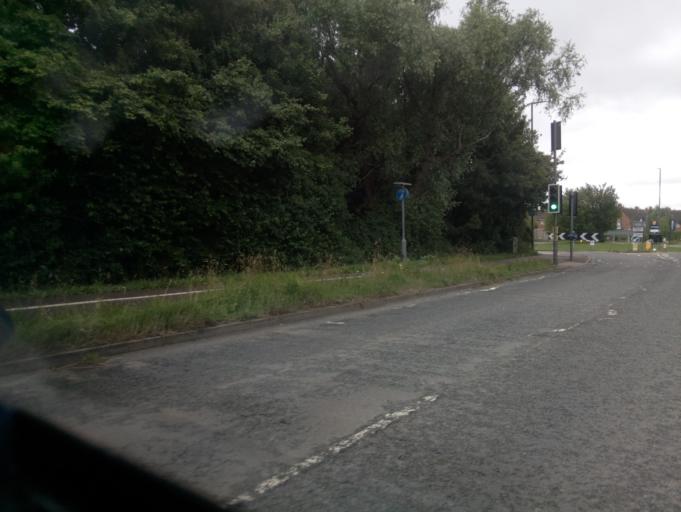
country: GB
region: England
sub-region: Gloucestershire
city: Tewkesbury
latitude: 51.9812
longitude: -2.1451
